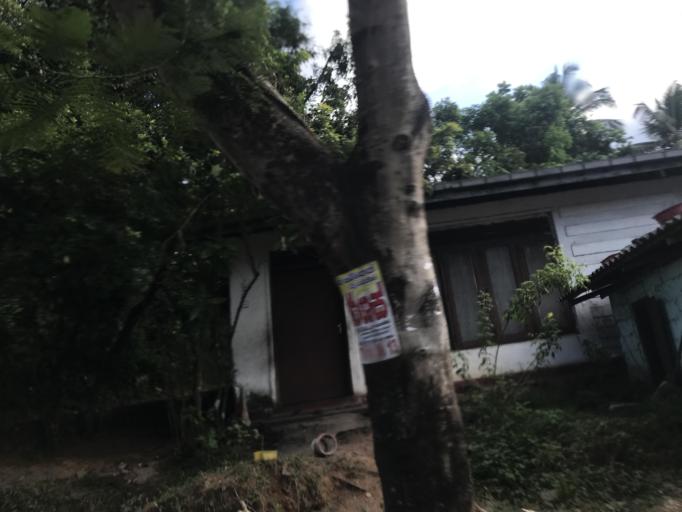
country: LK
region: Western
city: Gampaha
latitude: 7.0739
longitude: 79.9930
